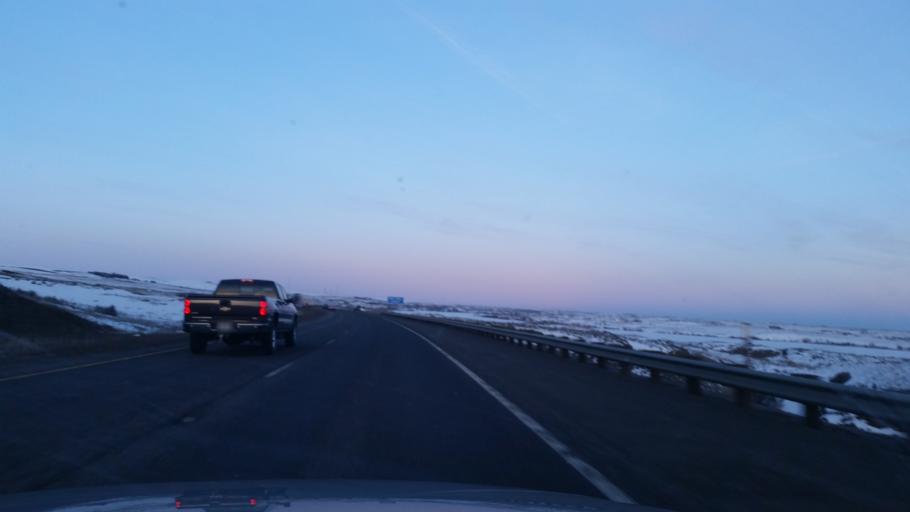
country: US
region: Washington
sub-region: Adams County
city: Ritzville
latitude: 47.2679
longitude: -118.0650
